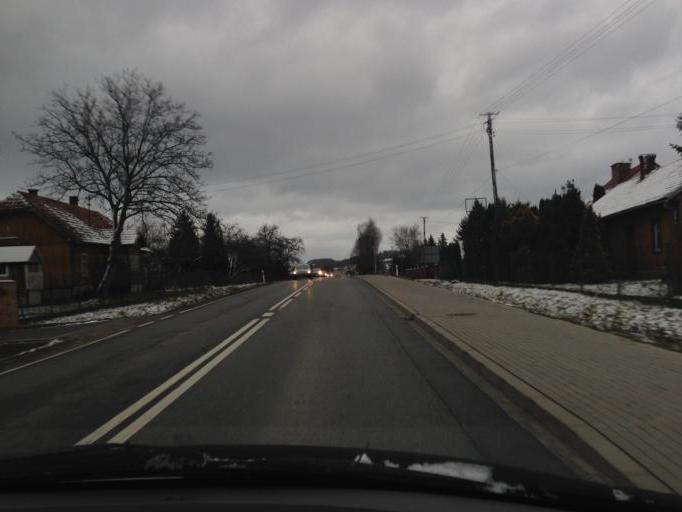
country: PL
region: Lesser Poland Voivodeship
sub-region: Powiat tarnowski
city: Zakliczyn
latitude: 49.8525
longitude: 20.8293
